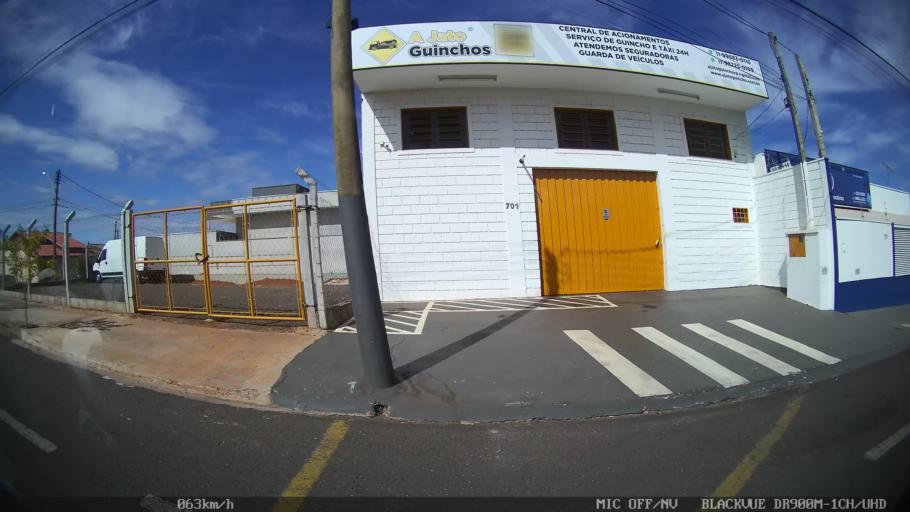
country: BR
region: Sao Paulo
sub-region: Sao Jose Do Rio Preto
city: Sao Jose do Rio Preto
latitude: -20.8416
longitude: -49.3604
